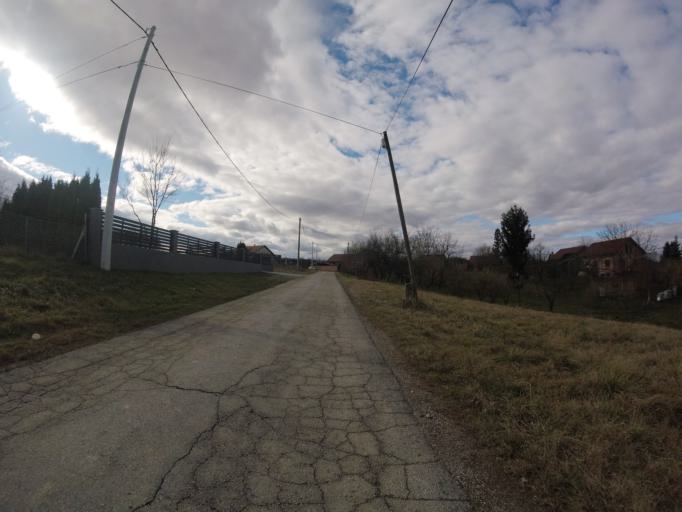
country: HR
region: Zagrebacka
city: Mraclin
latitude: 45.6320
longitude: 16.0526
